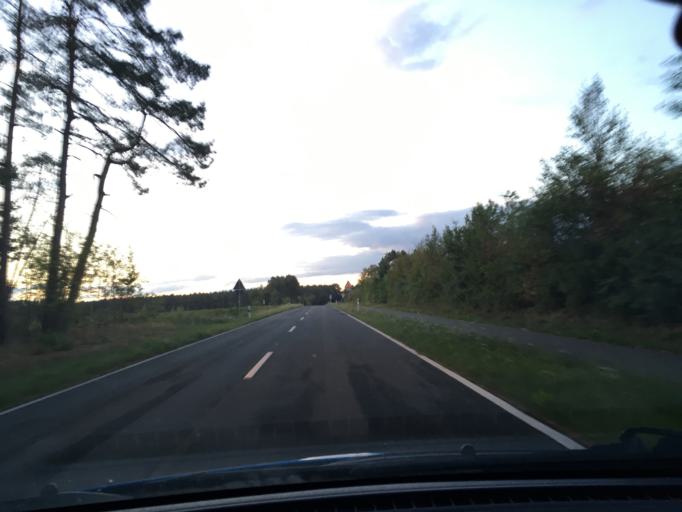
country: DE
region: Lower Saxony
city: Fassberg
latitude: 52.9138
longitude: 10.1506
